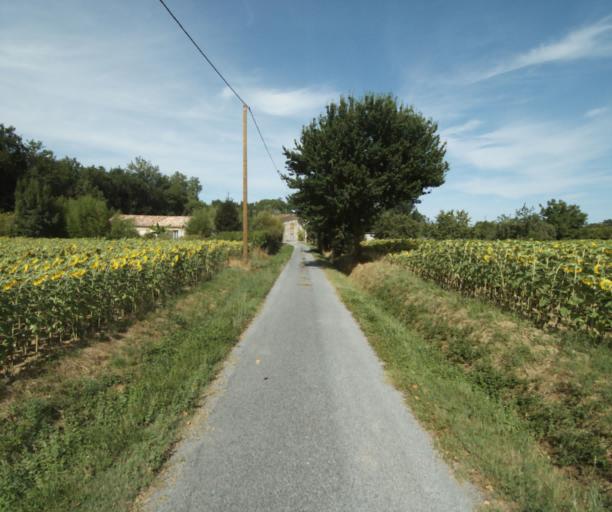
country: FR
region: Midi-Pyrenees
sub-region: Departement du Tarn
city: Soual
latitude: 43.5164
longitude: 2.0747
